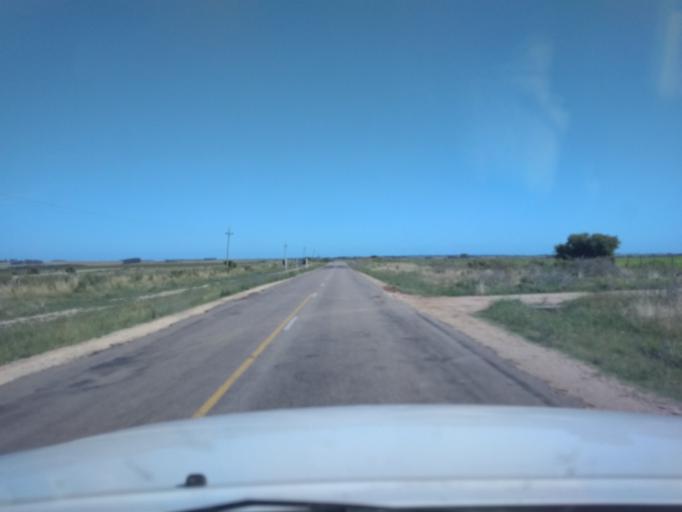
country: UY
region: Canelones
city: San Ramon
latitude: -34.2368
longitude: -55.9268
